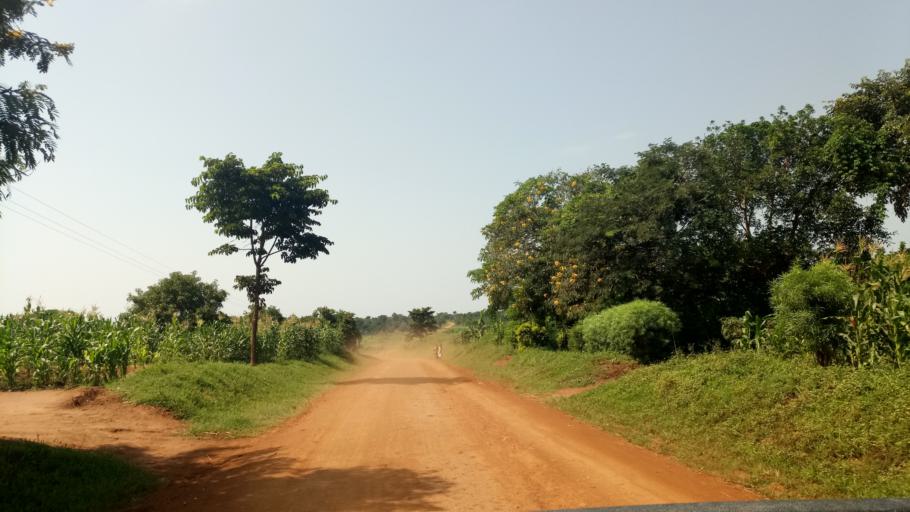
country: UG
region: Eastern Region
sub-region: Kaliro District
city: Kaliro
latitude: 0.9767
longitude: 33.4591
